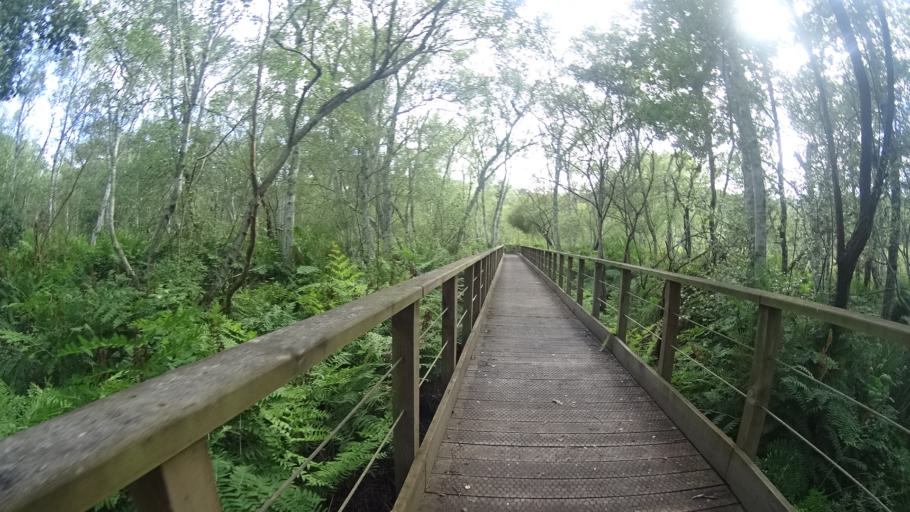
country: FR
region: Aquitaine
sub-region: Departement de la Gironde
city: Hourtin
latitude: 45.2190
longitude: -1.1273
